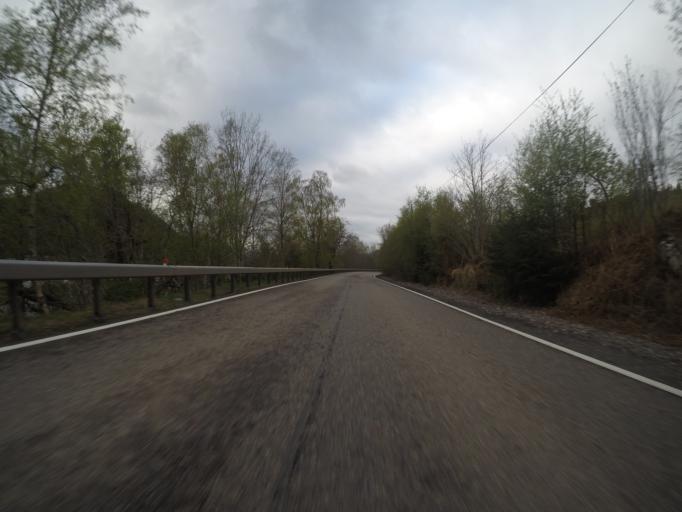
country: GB
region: Scotland
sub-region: Highland
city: Kingussie
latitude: 56.9567
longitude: -4.4731
